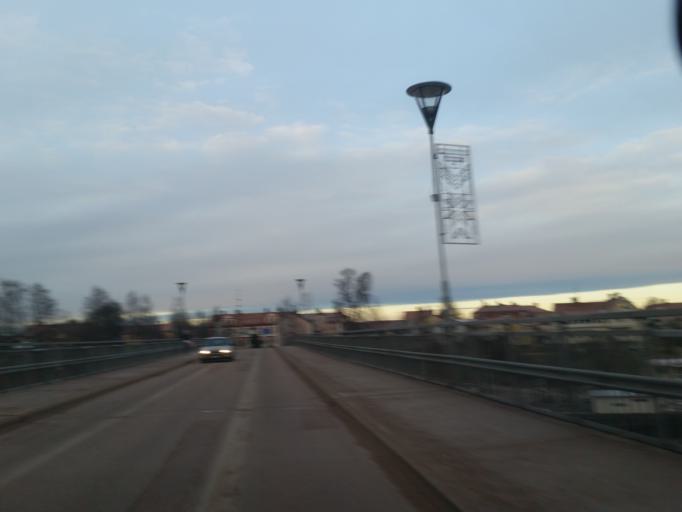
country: SE
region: Dalarna
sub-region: Leksand Municipality
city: Leksand
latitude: 60.7279
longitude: 14.9984
